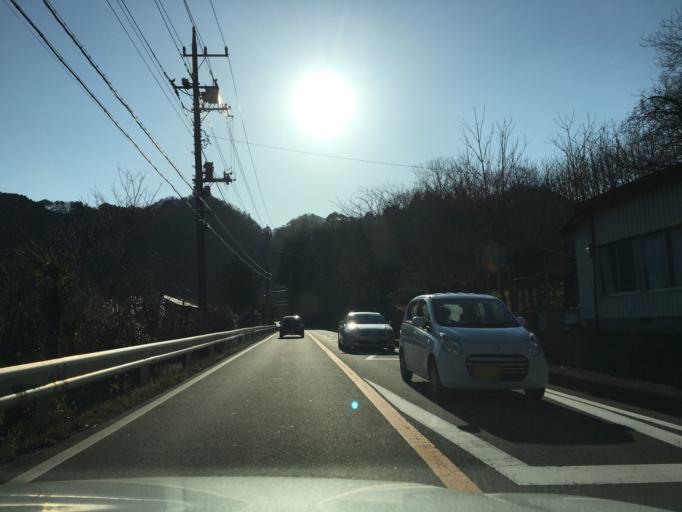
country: JP
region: Ibaraki
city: Daigo
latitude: 36.7370
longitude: 140.3848
